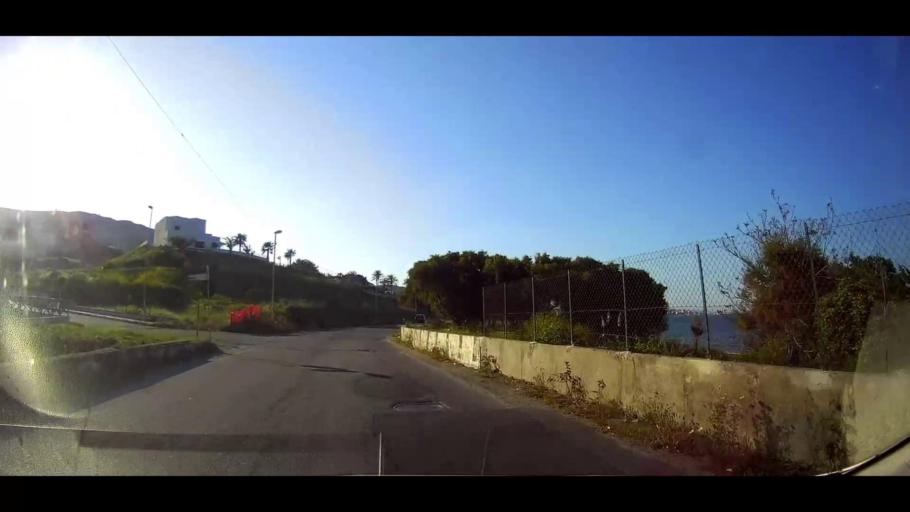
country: IT
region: Calabria
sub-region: Provincia di Crotone
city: Crotone
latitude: 39.0511
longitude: 17.1407
